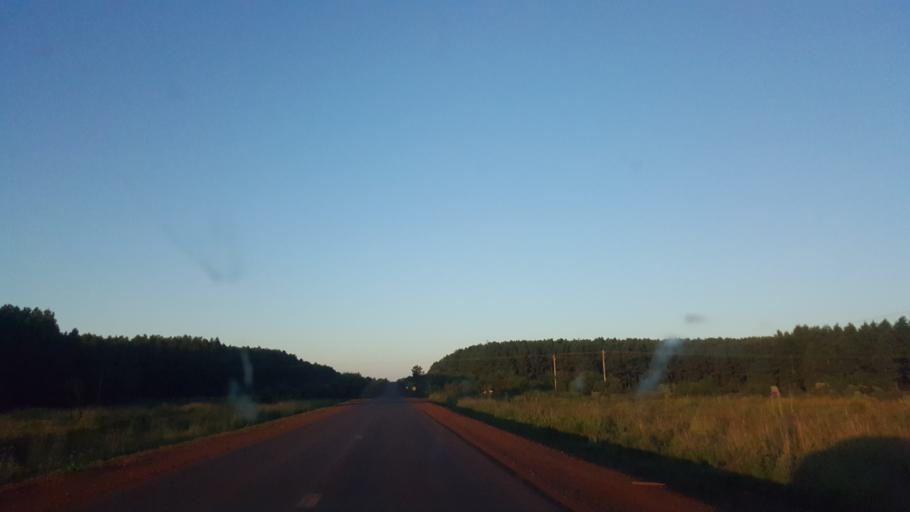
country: AR
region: Corrientes
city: Santo Tome
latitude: -28.4247
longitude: -55.9914
